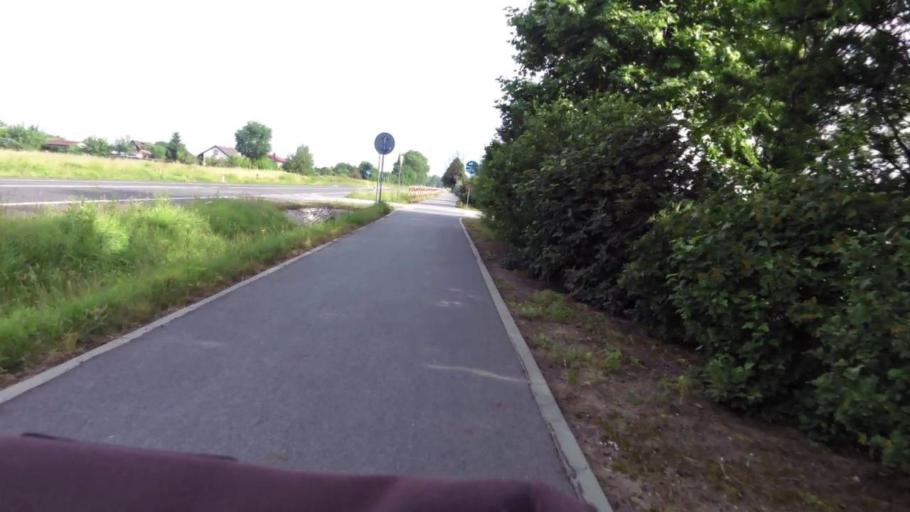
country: PL
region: West Pomeranian Voivodeship
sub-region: Powiat kamienski
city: Dziwnow
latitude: 54.0199
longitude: 14.8105
